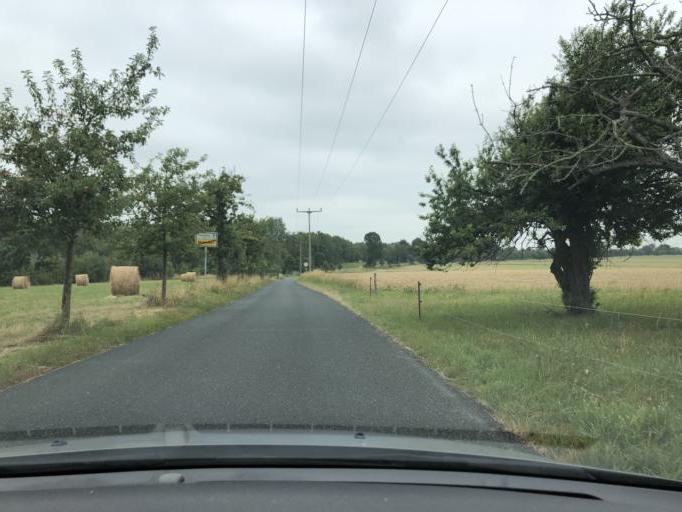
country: DE
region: Saxony
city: Frohburg
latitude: 51.0897
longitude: 12.5609
